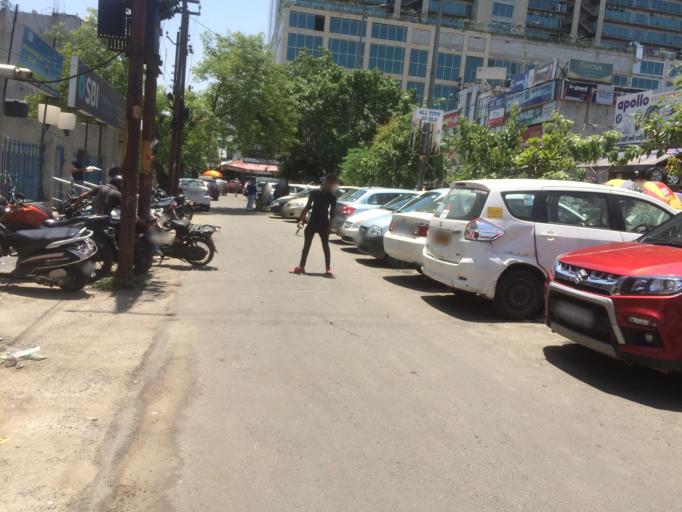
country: IN
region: Uttar Pradesh
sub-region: Gautam Buddha Nagar
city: Noida
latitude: 28.5782
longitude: 77.3165
